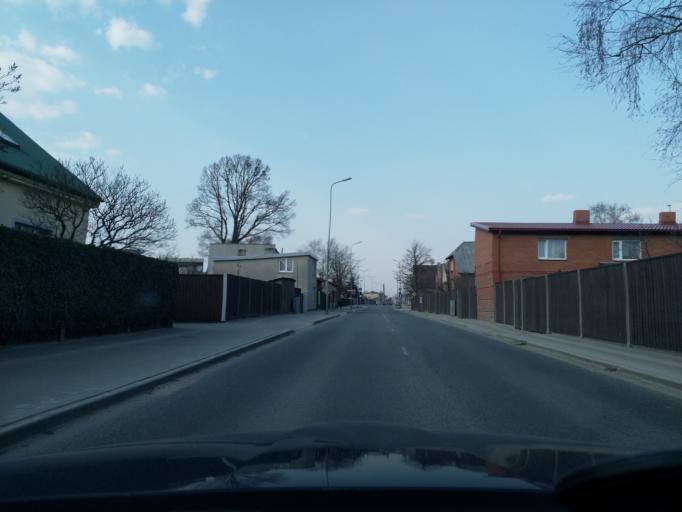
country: LV
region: Liepaja
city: Liepaja
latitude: 56.4993
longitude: 21.0211
